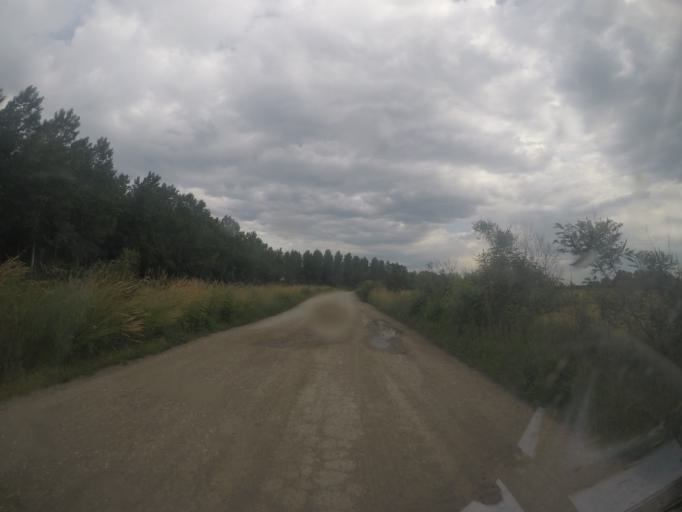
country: RS
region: Central Serbia
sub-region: Belgrade
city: Zemun
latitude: 44.8754
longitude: 20.3837
